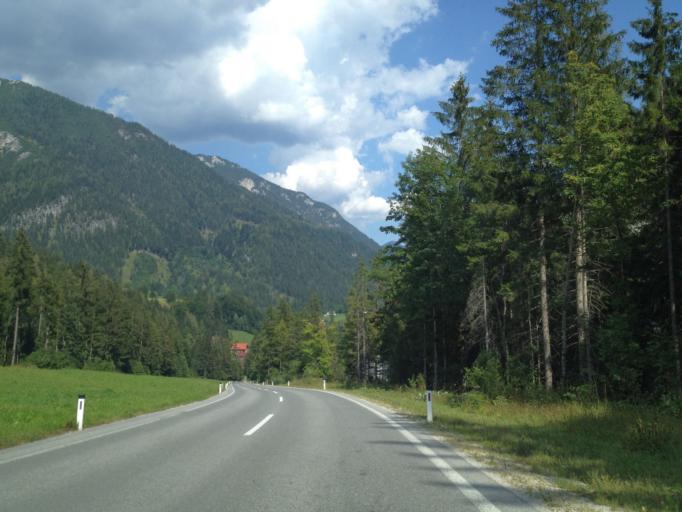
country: AT
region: Styria
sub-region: Politischer Bezirk Liezen
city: Schladming
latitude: 47.4253
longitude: 13.7060
